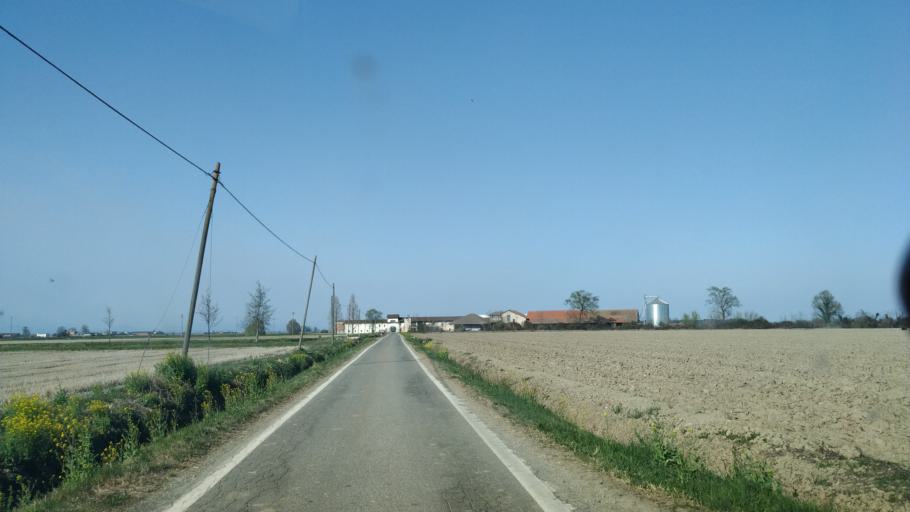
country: IT
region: Piedmont
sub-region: Provincia di Vercelli
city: Salasco
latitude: 45.3354
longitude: 8.2574
